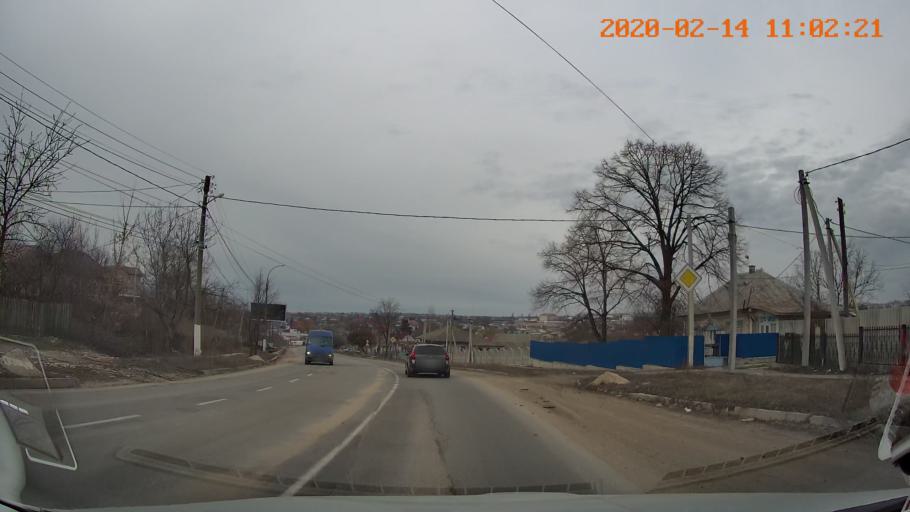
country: MD
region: Raionul Edinet
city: Edinet
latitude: 48.1640
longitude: 27.3203
